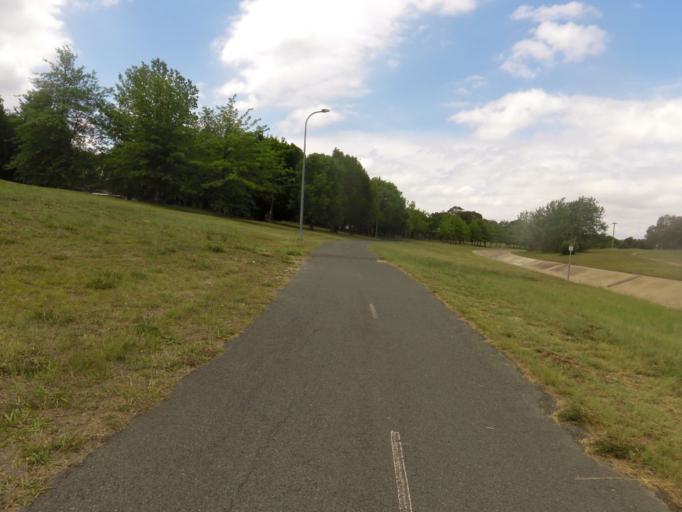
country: AU
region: Australian Capital Territory
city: Macarthur
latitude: -35.4205
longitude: 149.1052
